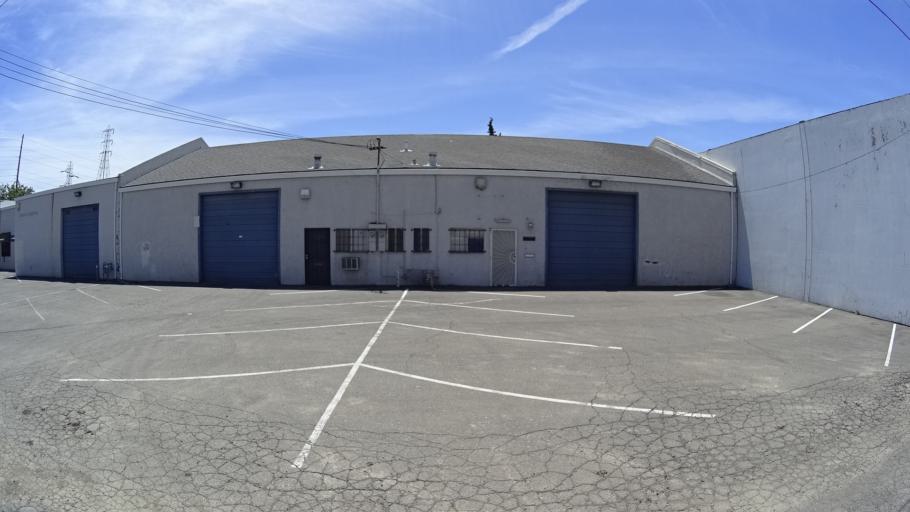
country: US
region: California
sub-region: Sacramento County
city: Florin
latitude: 38.5341
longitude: -121.4101
